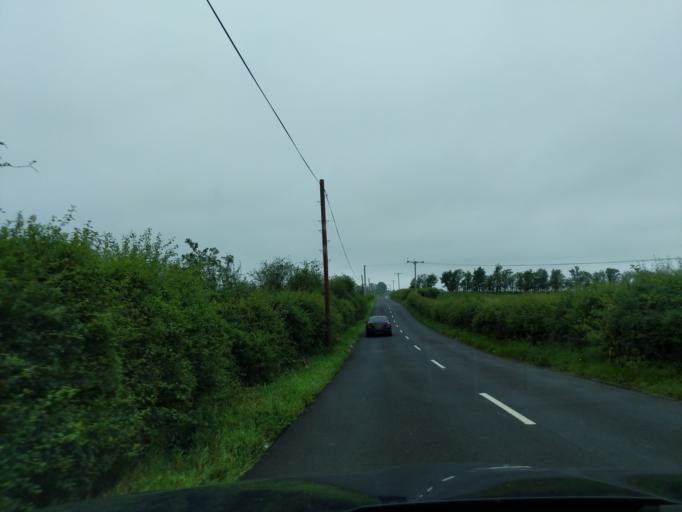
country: GB
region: England
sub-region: Northumberland
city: Lowick
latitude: 55.6563
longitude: -1.9515
